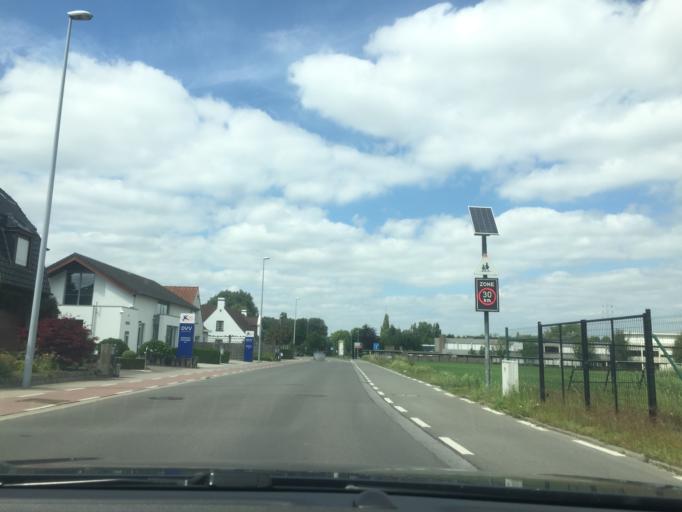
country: BE
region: Flanders
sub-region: Provincie West-Vlaanderen
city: Izegem
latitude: 50.9174
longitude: 3.2299
